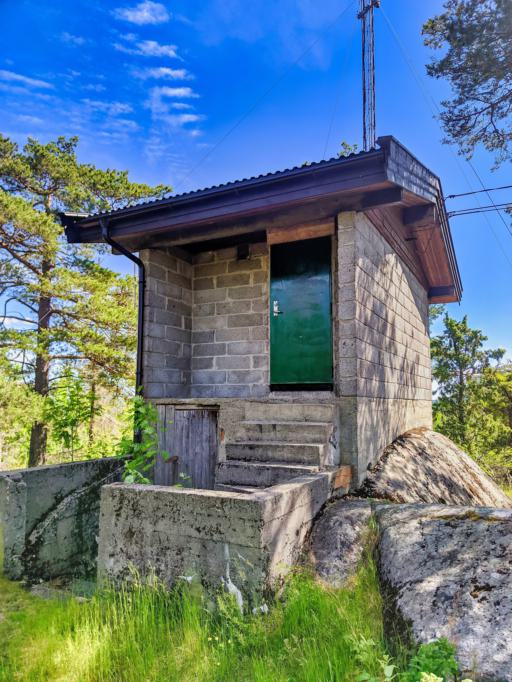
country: NO
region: Ostfold
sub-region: Eidsberg
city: Mysen
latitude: 59.5638
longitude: 11.3432
